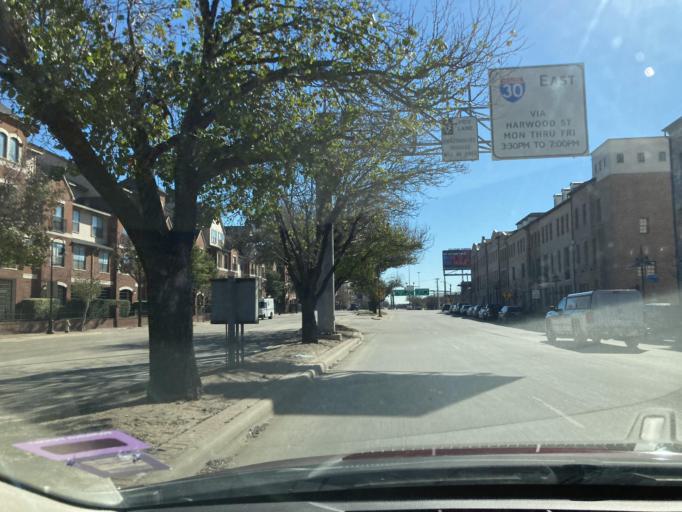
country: US
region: Texas
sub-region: Dallas County
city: Dallas
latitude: 32.7799
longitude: -96.7896
